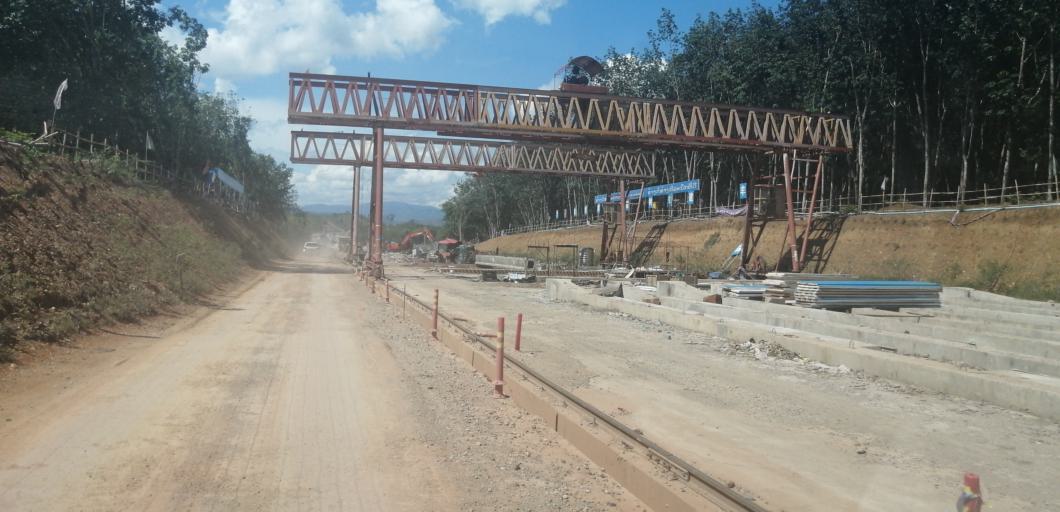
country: LA
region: Vientiane
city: Vangviang
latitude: 18.7481
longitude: 102.3843
